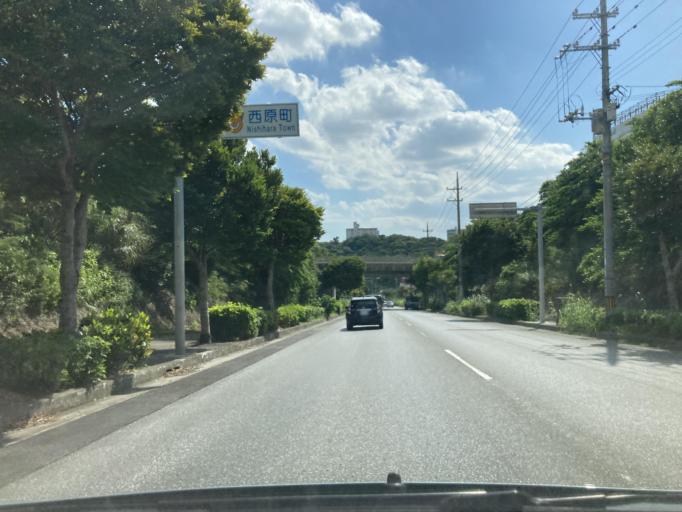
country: JP
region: Okinawa
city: Ginowan
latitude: 26.2502
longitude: 127.7576
